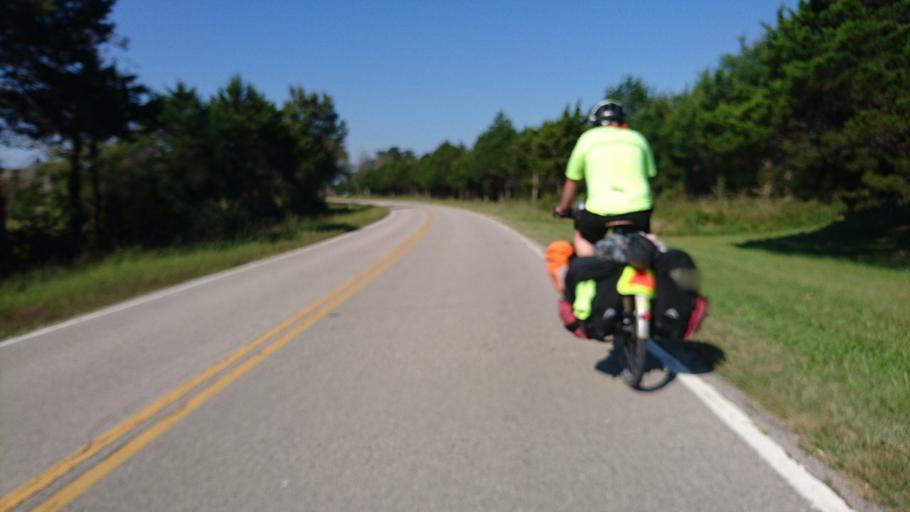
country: US
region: Missouri
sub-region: Pulaski County
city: Richland
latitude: 37.7663
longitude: -92.3868
